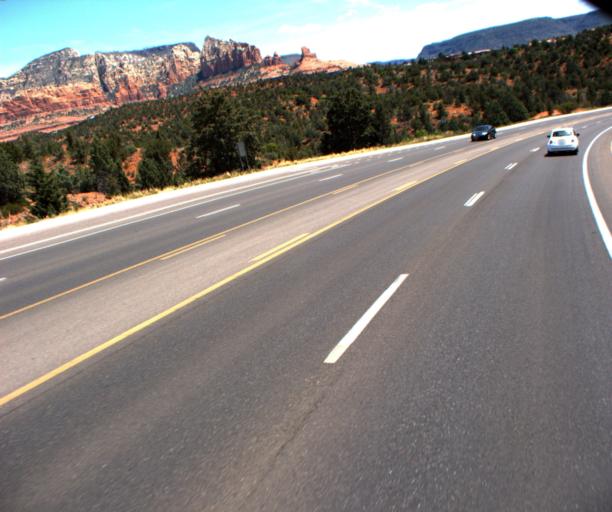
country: US
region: Arizona
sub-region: Coconino County
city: Sedona
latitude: 34.8669
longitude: -111.7730
